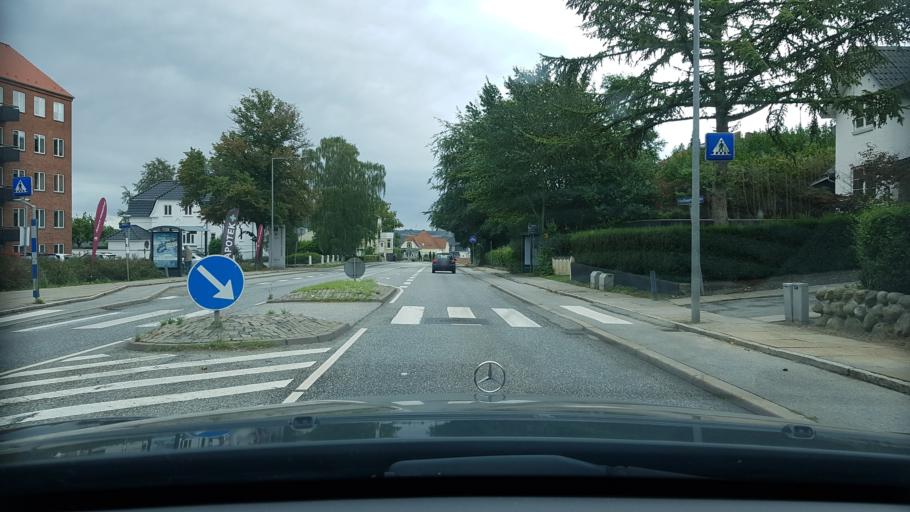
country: DK
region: Central Jutland
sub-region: Randers Kommune
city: Randers
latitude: 56.4697
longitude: 10.0455
